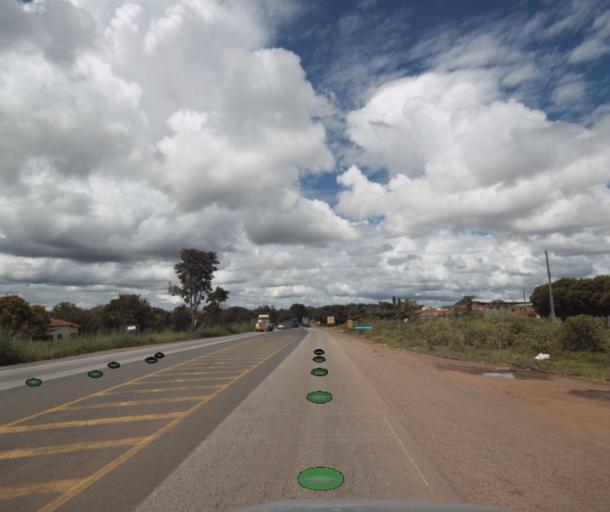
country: BR
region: Goias
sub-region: Uruacu
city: Uruacu
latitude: -14.3159
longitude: -49.1503
